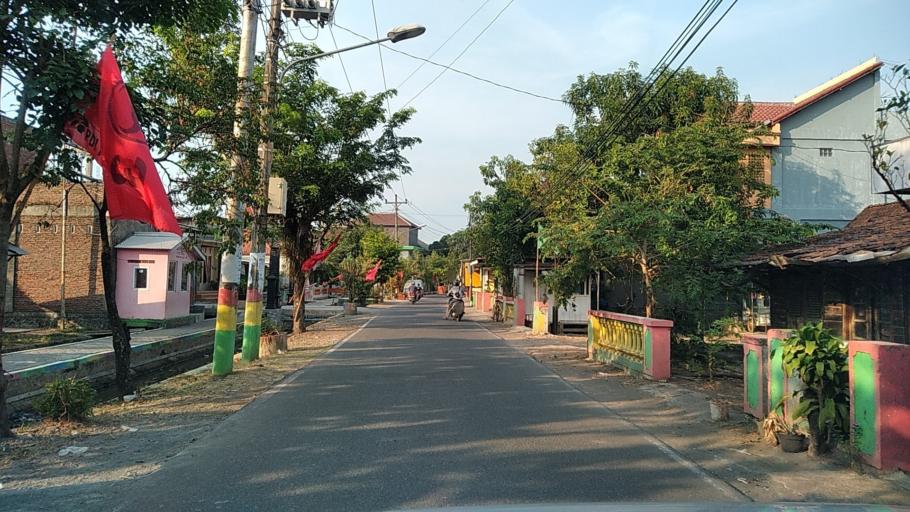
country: ID
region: Central Java
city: Semarang
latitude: -6.9725
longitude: 110.2962
